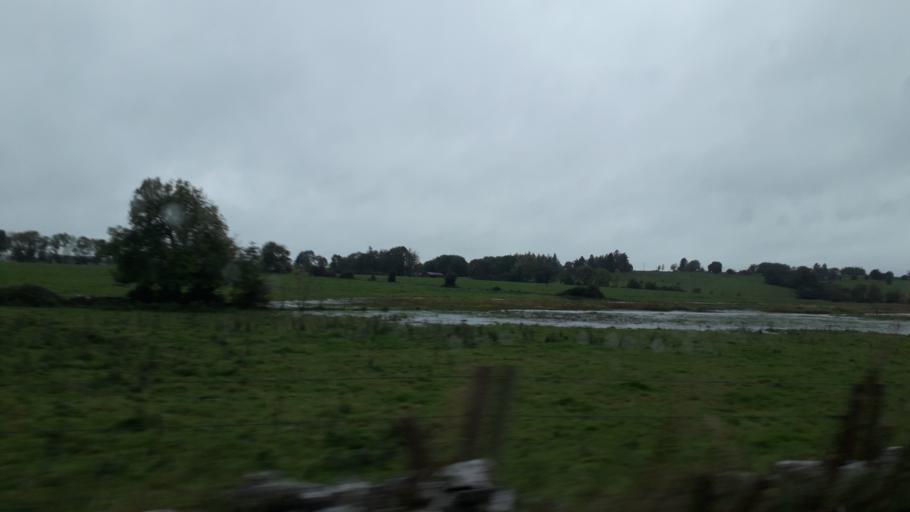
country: IE
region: Connaught
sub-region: Roscommon
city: Roscommon
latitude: 53.7704
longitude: -8.2242
